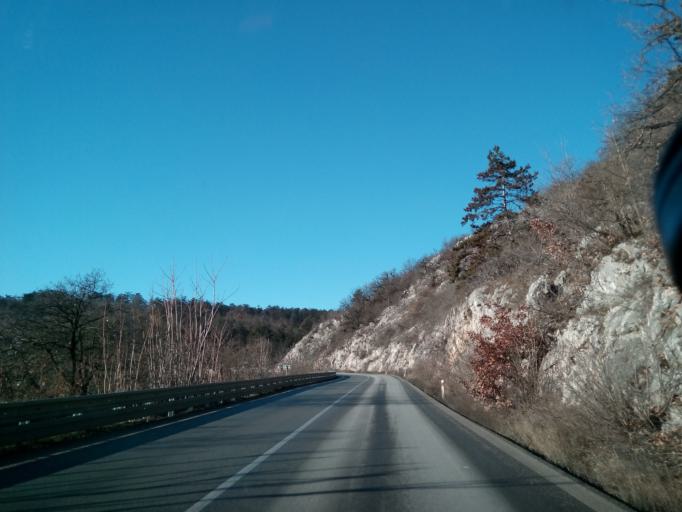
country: SK
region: Kosicky
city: Roznava
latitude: 48.6027
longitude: 20.6435
